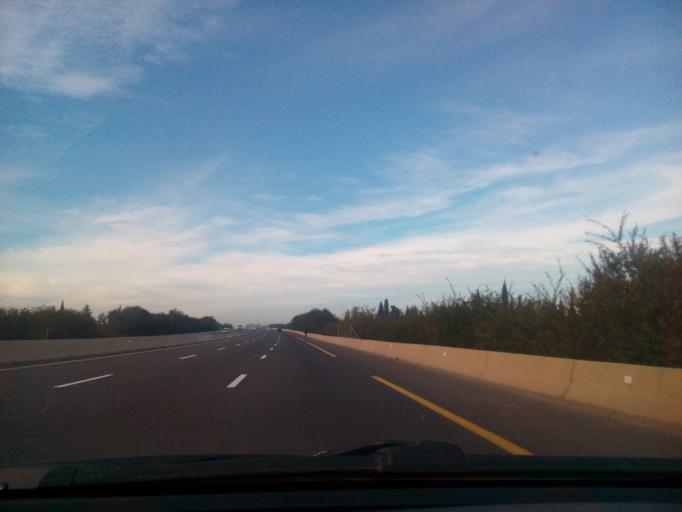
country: DZ
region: Mascara
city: Mascara
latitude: 35.6218
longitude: 0.0517
